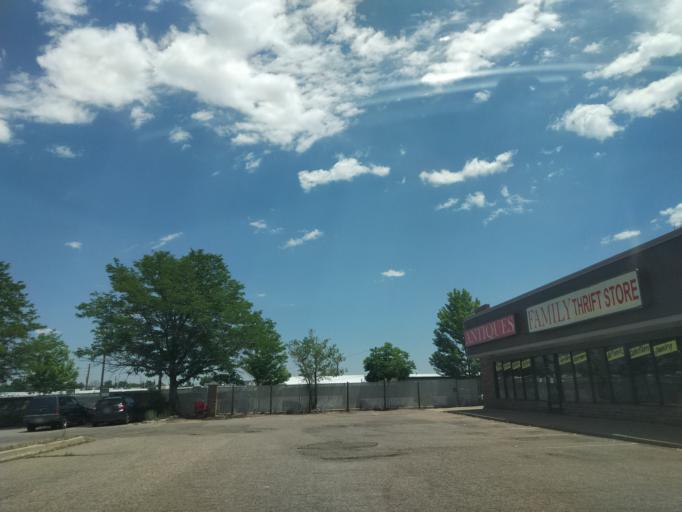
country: US
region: Colorado
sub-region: Jefferson County
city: Lakewood
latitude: 39.6812
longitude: -105.0851
